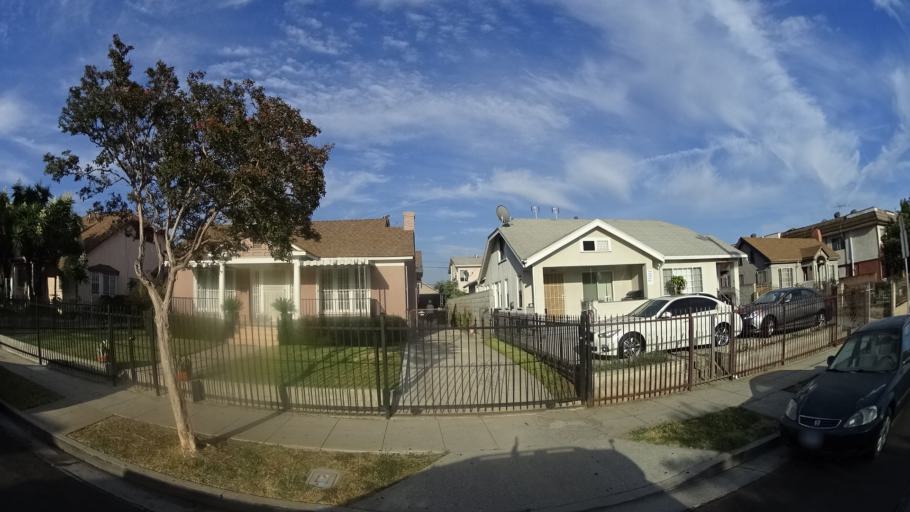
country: US
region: California
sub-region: Los Angeles County
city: Silver Lake
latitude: 34.0919
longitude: -118.2974
